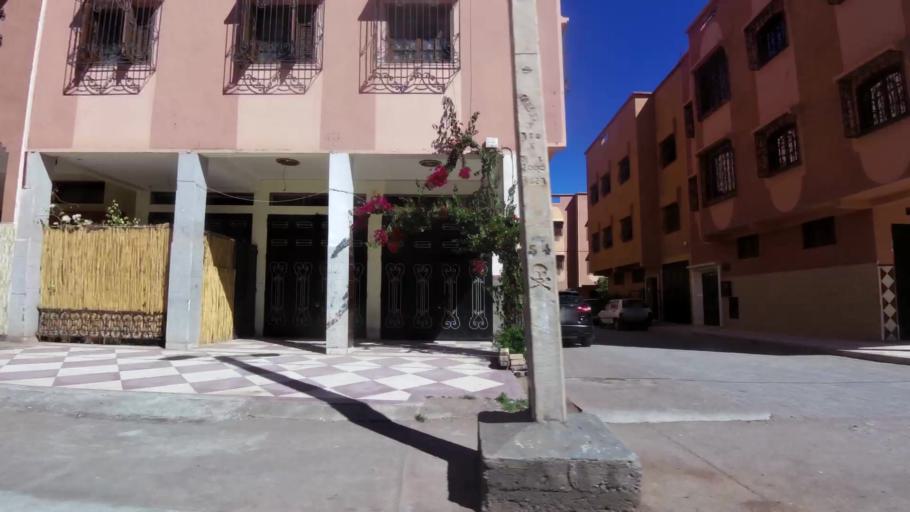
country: MA
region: Marrakech-Tensift-Al Haouz
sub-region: Marrakech
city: Marrakesh
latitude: 31.5940
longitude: -8.0483
